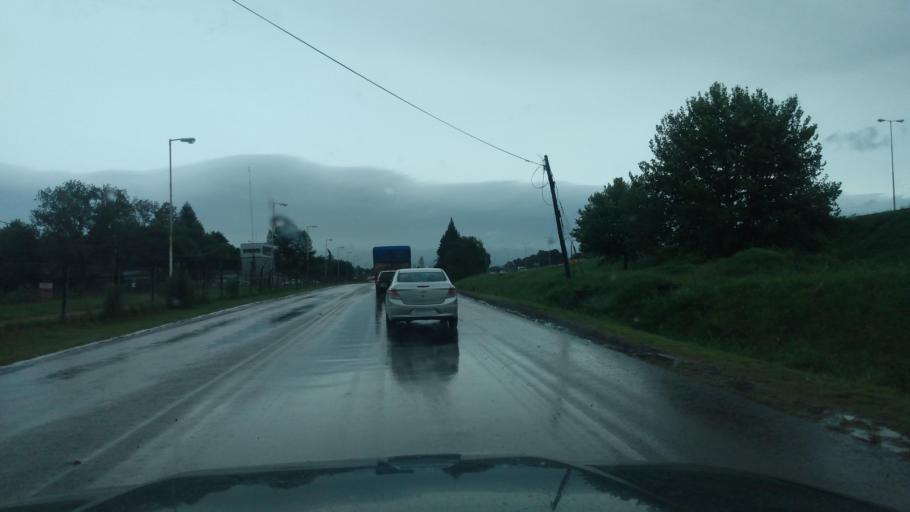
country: AR
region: Buenos Aires
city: Capilla del Senor
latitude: -34.3917
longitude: -59.0352
